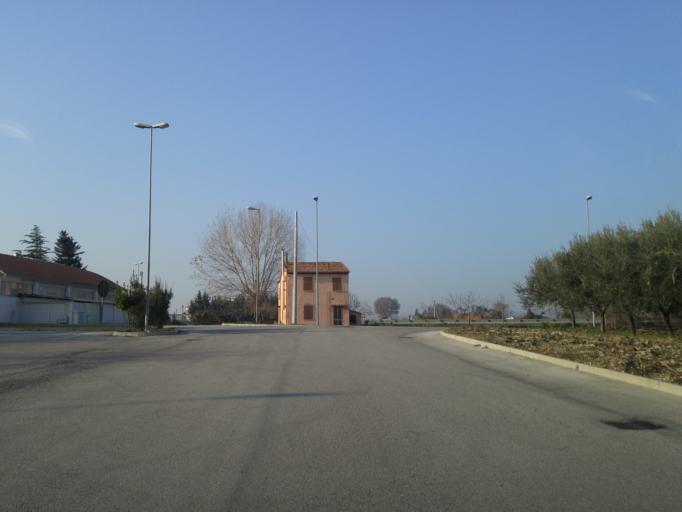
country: IT
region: The Marches
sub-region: Provincia di Pesaro e Urbino
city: Lucrezia
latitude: 43.7666
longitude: 12.9546
